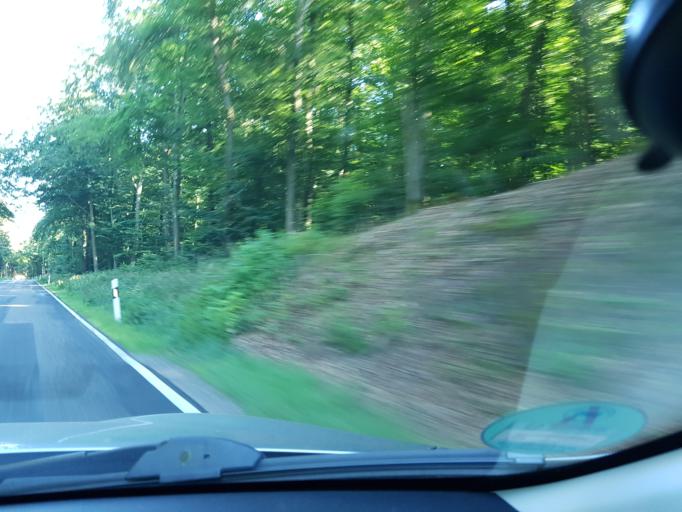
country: DE
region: Rheinland-Pfalz
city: Arzbach
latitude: 50.4031
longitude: 7.7773
